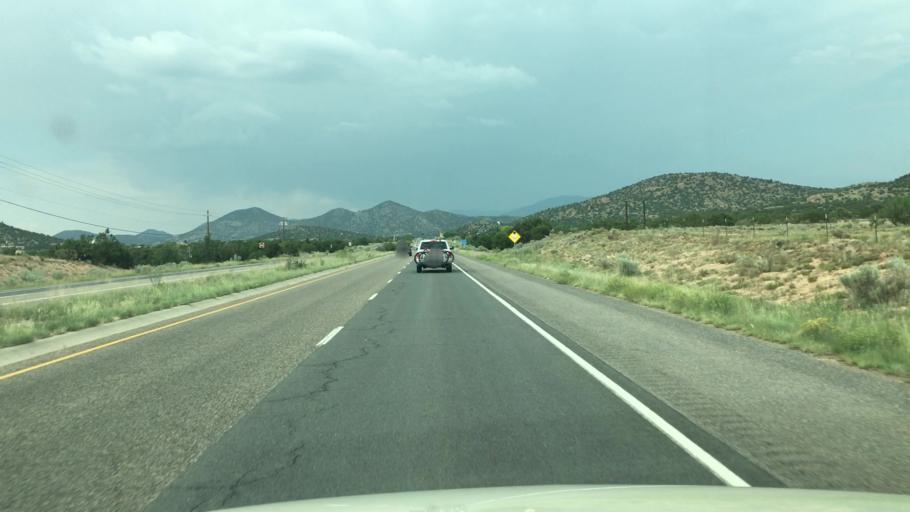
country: US
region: New Mexico
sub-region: Santa Fe County
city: Eldorado at Santa Fe
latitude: 35.5311
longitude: -105.8889
